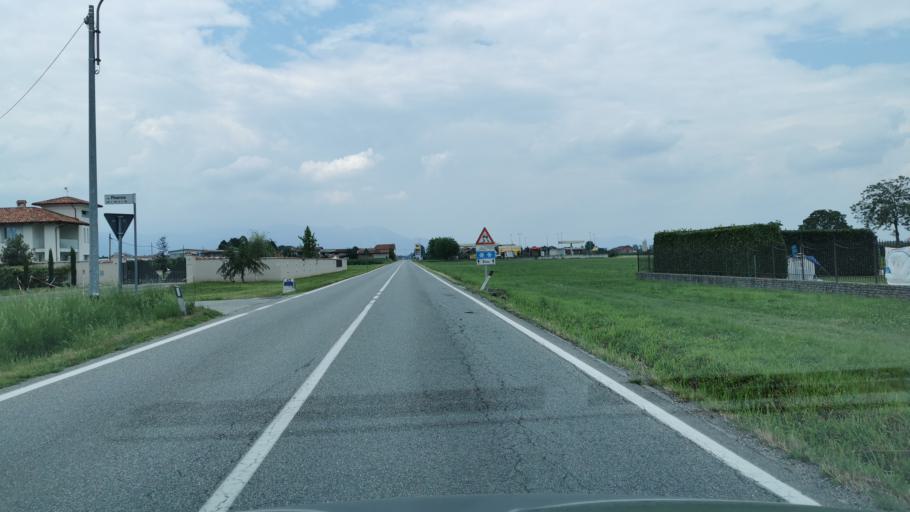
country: IT
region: Piedmont
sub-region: Provincia di Torino
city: Cavour
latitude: 44.8039
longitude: 7.3732
